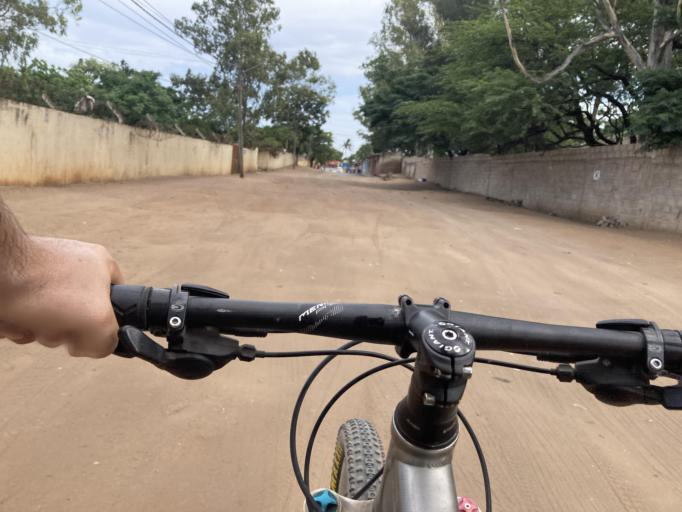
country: MZ
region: Maputo City
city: Maputo
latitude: -25.9307
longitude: 32.5843
